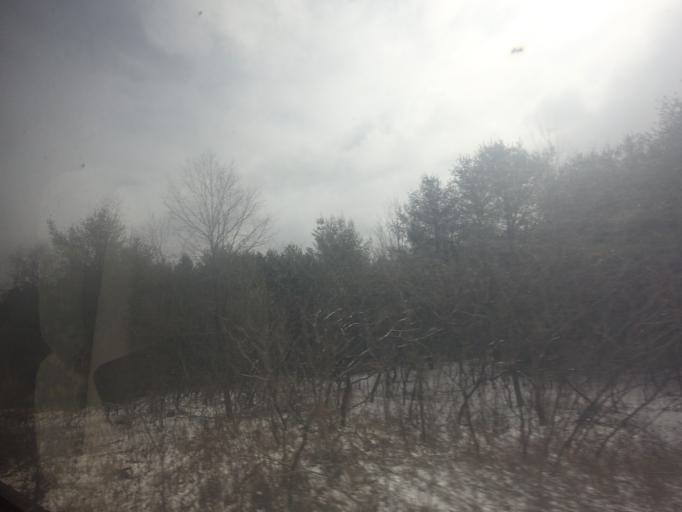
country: CA
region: Ontario
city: Cobourg
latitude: 43.9387
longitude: -78.3948
